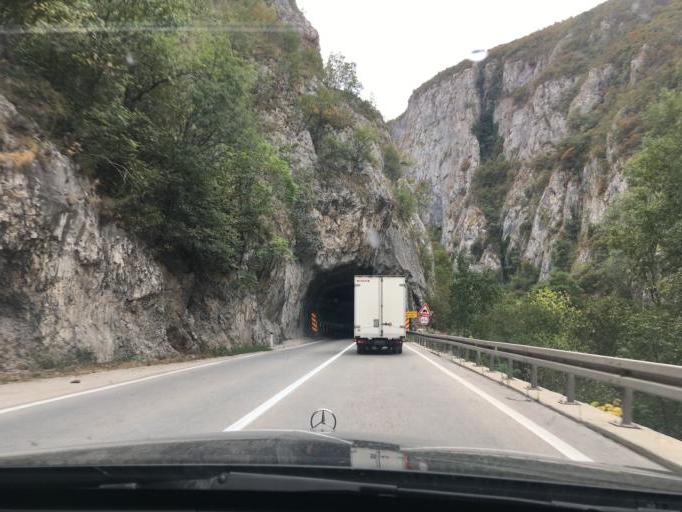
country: RS
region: Central Serbia
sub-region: Nisavski Okrug
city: Svrljig
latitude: 43.3198
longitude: 22.1731
